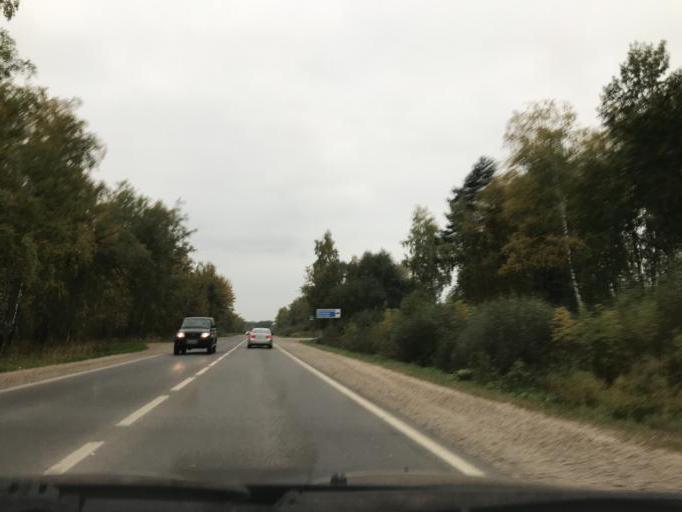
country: RU
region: Kaluga
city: Kaluga
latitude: 54.6120
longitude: 36.2746
